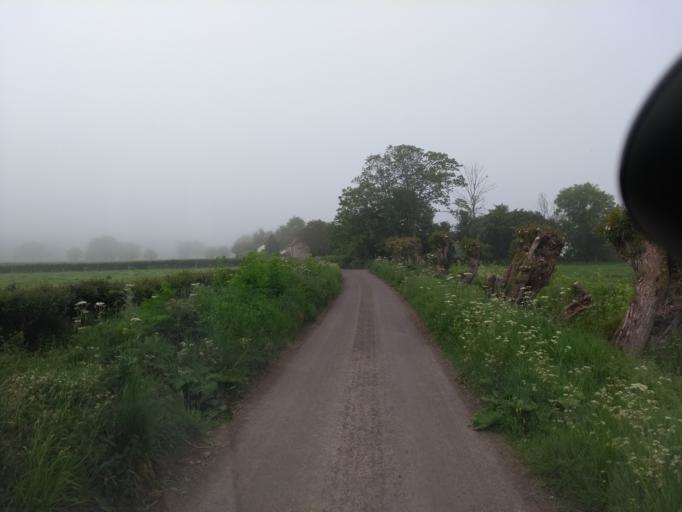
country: GB
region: England
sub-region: Somerset
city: Creech Saint Michael
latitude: 50.9948
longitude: -2.9913
